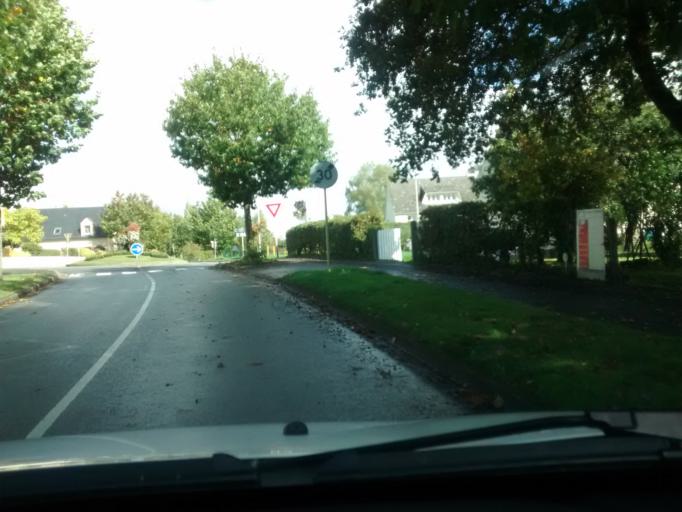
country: FR
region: Brittany
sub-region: Departement d'Ille-et-Vilaine
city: Servon-sur-Vilaine
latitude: 48.1197
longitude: -1.4572
